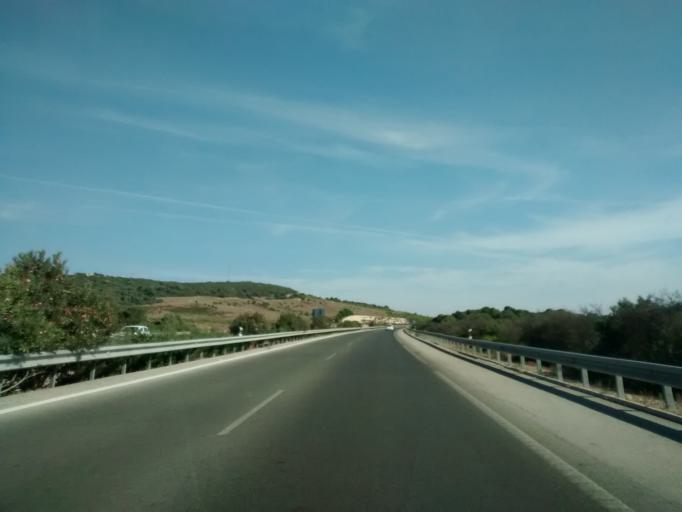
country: ES
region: Andalusia
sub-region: Provincia de Cadiz
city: Conil de la Frontera
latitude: 36.3166
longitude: -6.0572
